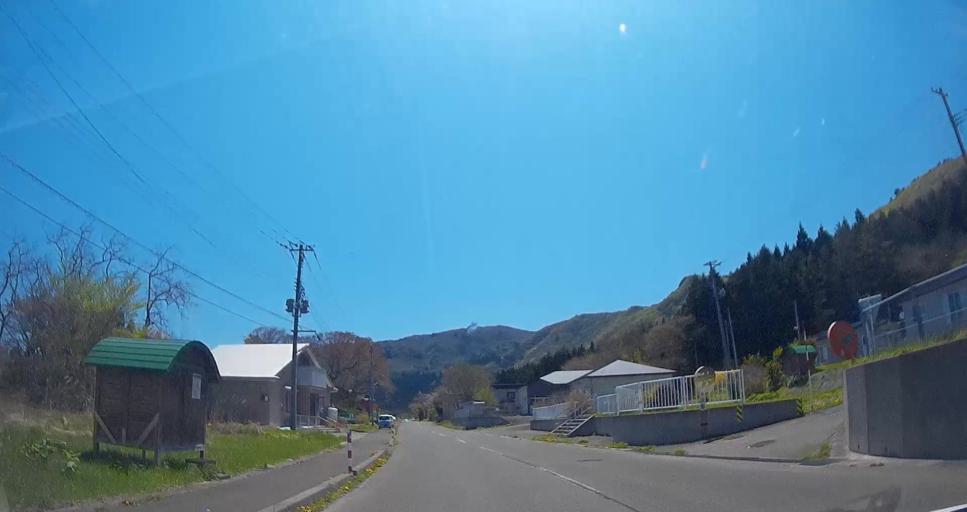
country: JP
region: Aomori
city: Mutsu
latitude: 41.4076
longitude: 141.4469
